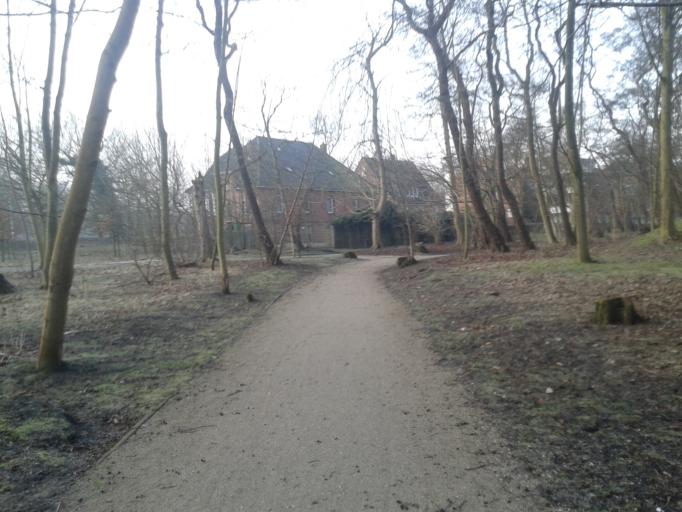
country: DE
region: Lower Saxony
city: Norderney
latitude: 53.7064
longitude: 7.1551
